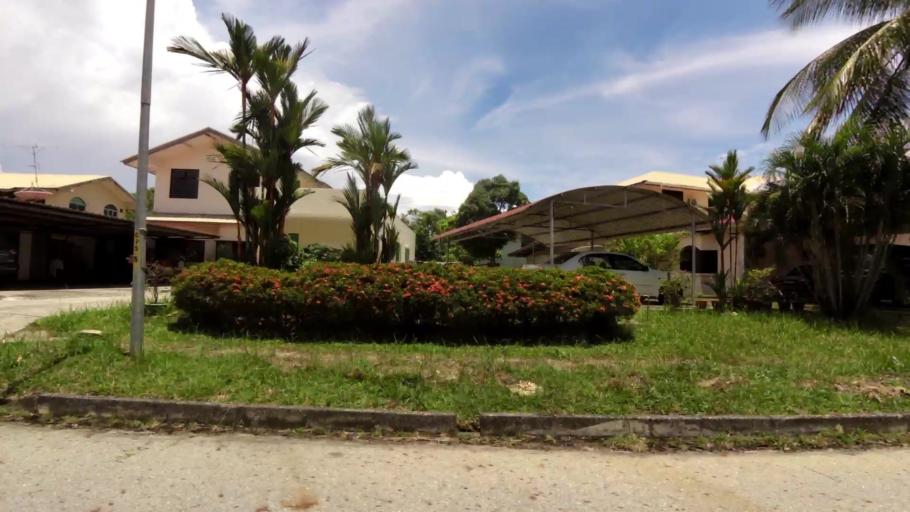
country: BN
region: Brunei and Muara
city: Bandar Seri Begawan
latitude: 4.9631
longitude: 114.9175
